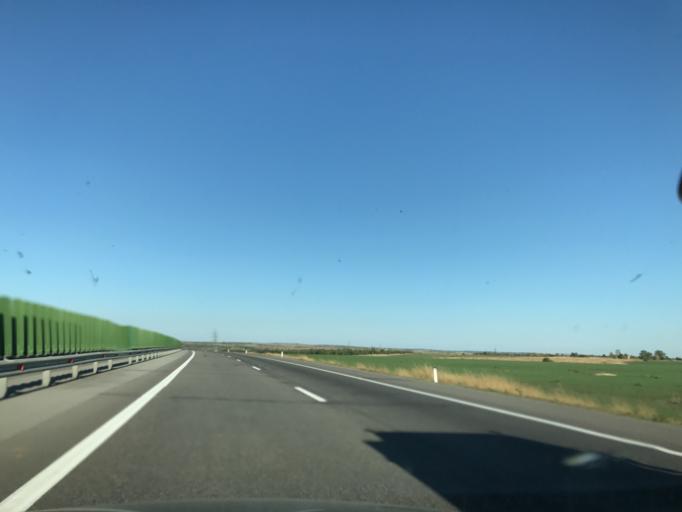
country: RU
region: Rostov
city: Tarasovskiy
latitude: 48.7438
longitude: 40.3925
